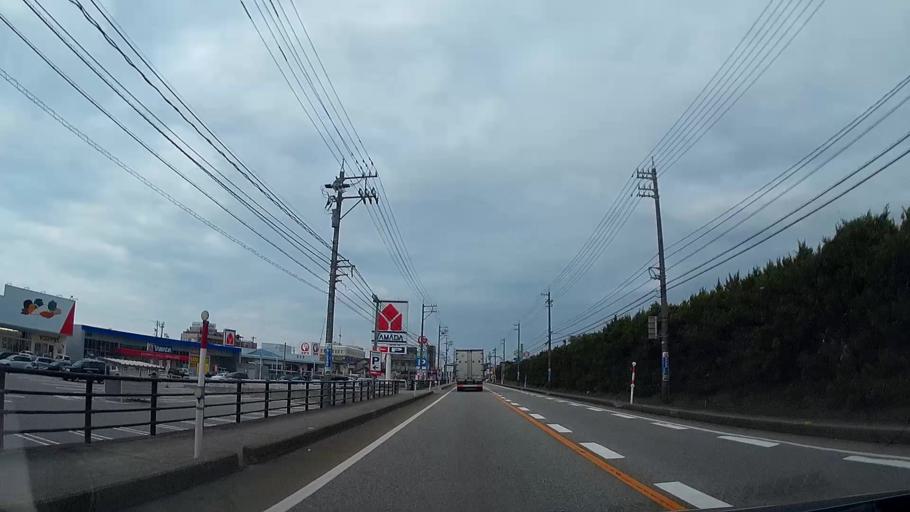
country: JP
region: Toyama
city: Nyuzen
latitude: 36.9310
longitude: 137.5002
